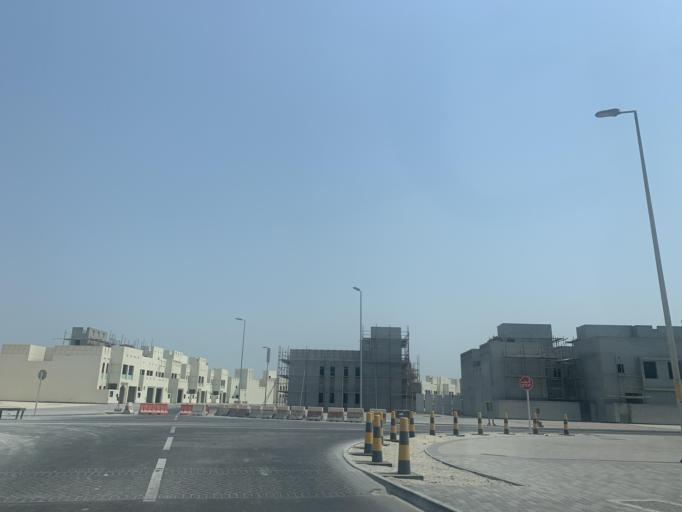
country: BH
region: Muharraq
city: Al Hadd
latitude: 26.2400
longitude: 50.6655
